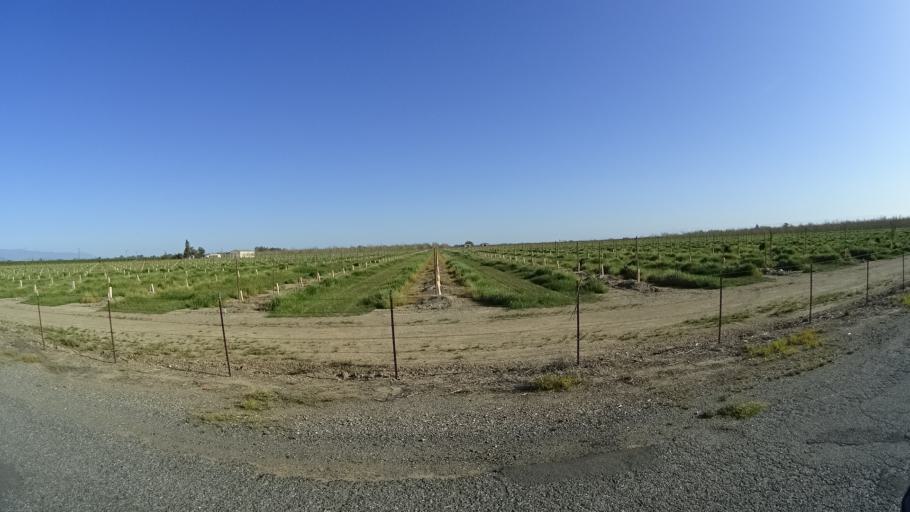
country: US
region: California
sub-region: Glenn County
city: Orland
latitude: 39.6823
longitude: -122.1752
